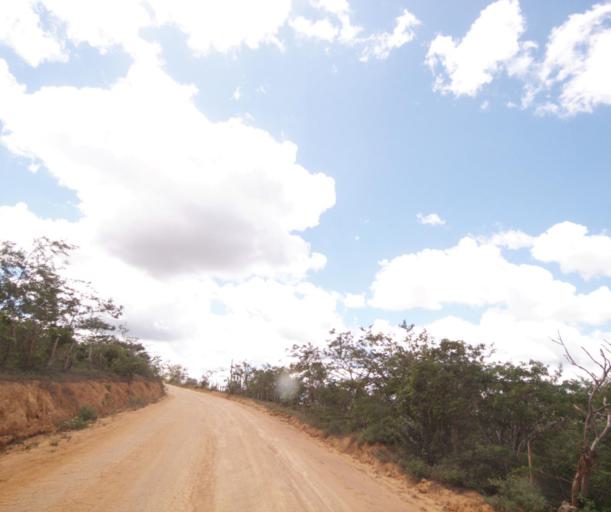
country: BR
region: Bahia
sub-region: Pocoes
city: Pocoes
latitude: -14.3899
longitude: -40.5454
